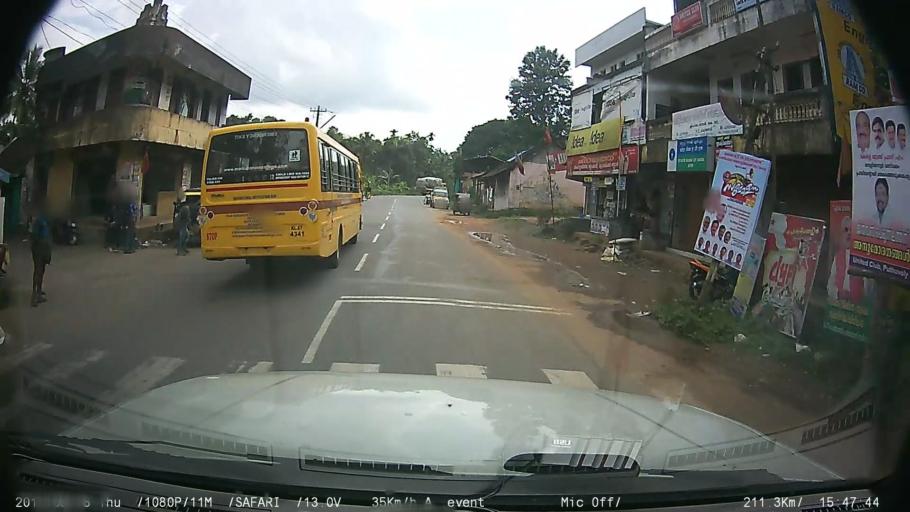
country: IN
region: Kerala
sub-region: Kottayam
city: Palackattumala
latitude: 9.8306
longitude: 76.5934
